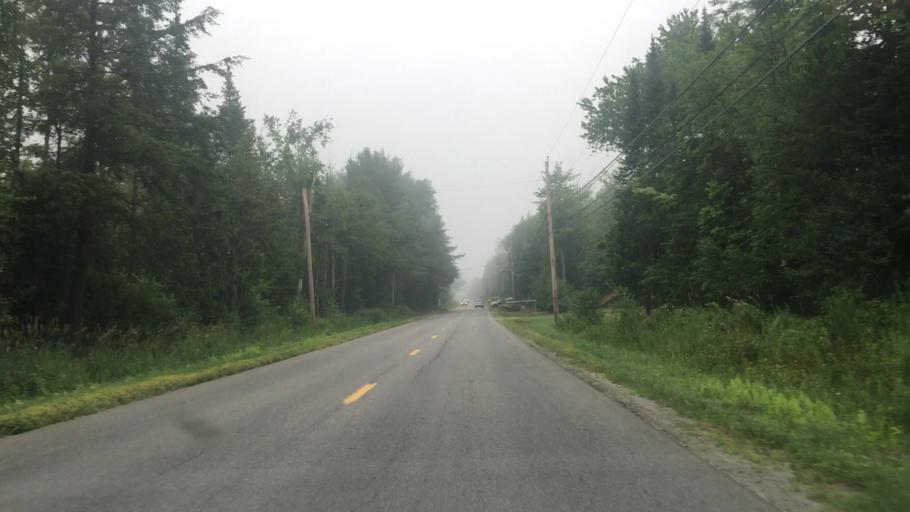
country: US
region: Maine
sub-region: Kennebec County
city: Oakland
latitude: 44.5194
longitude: -69.7273
